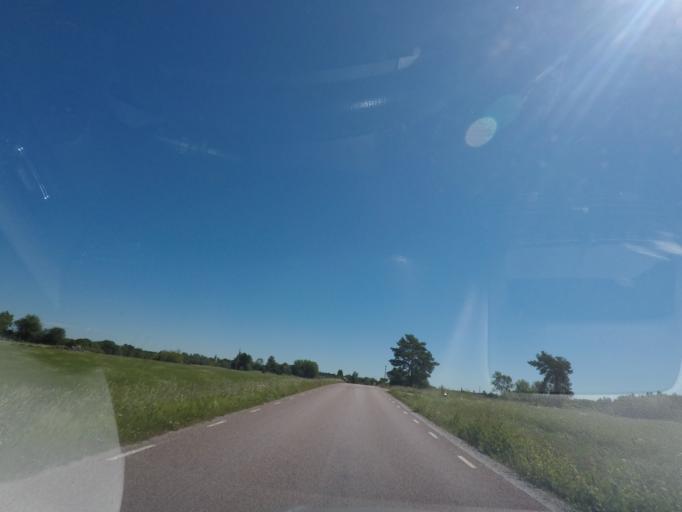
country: SE
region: Uppsala
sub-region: Enkopings Kommun
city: Irsta
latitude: 59.6805
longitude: 16.8294
